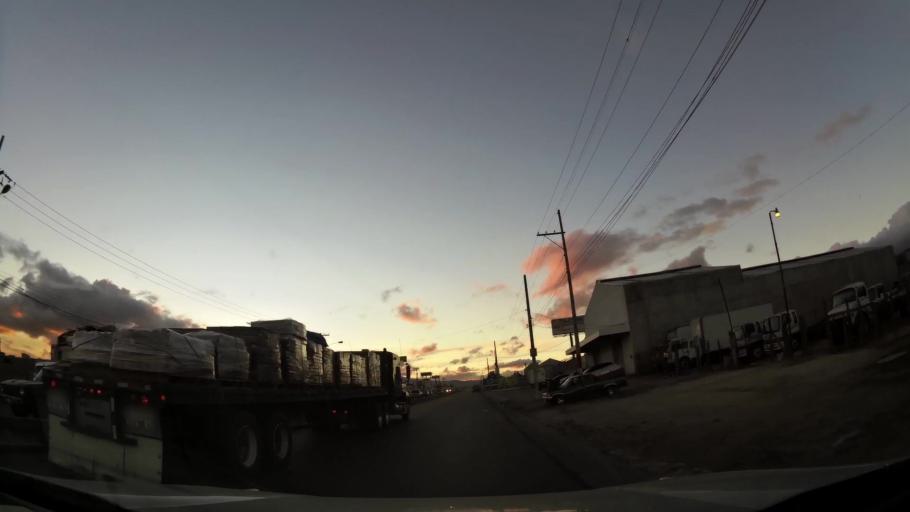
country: GT
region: Quetzaltenango
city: Quetzaltenango
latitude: 14.8584
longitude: -91.5130
